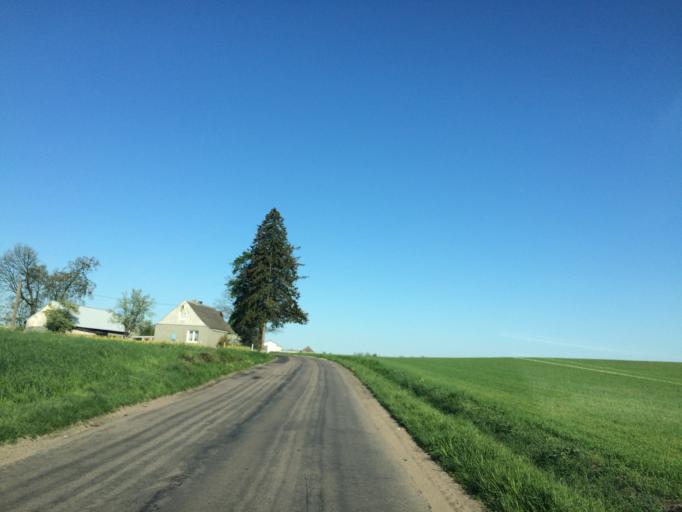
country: PL
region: Warmian-Masurian Voivodeship
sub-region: Powiat dzialdowski
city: Rybno
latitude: 53.3869
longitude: 19.9171
